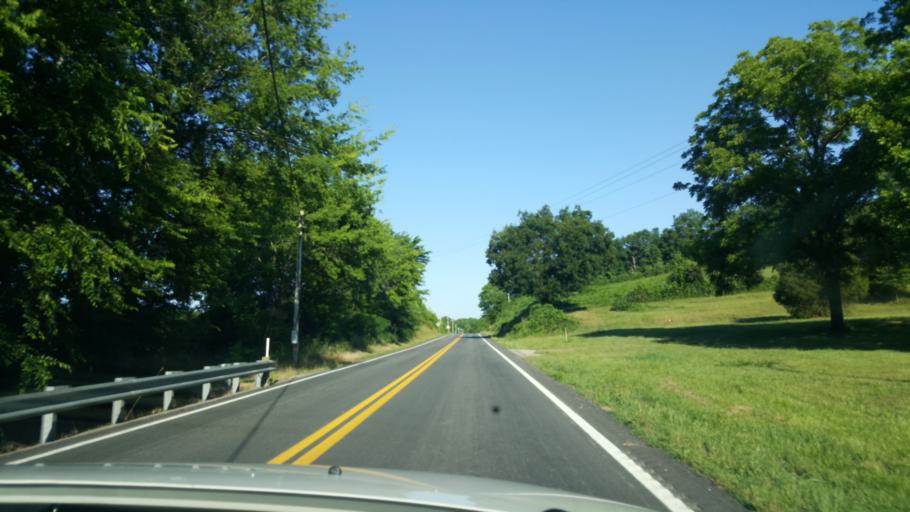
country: US
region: Tennessee
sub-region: Lawrence County
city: Lawrenceburg
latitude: 35.3985
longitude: -87.3746
